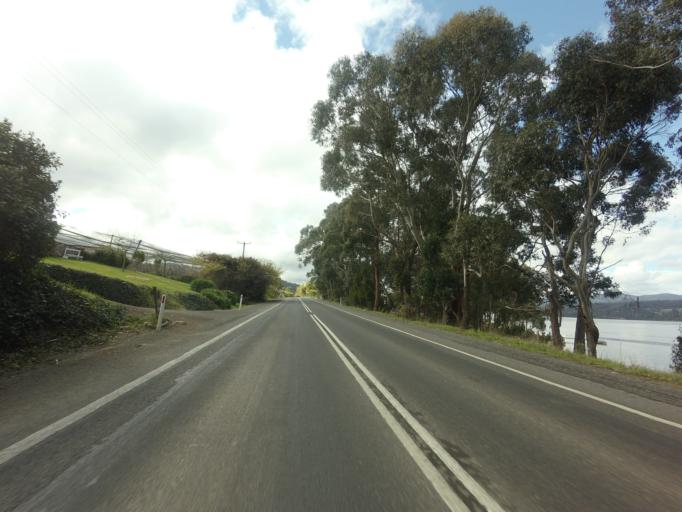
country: AU
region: Tasmania
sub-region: Huon Valley
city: Geeveston
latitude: -43.1472
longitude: 146.9779
